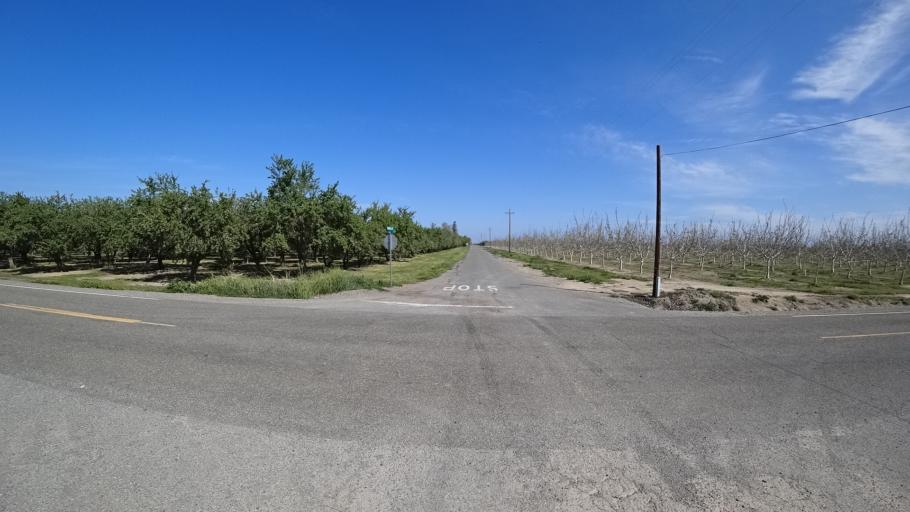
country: US
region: California
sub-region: Glenn County
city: Hamilton City
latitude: 39.6306
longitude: -122.0181
